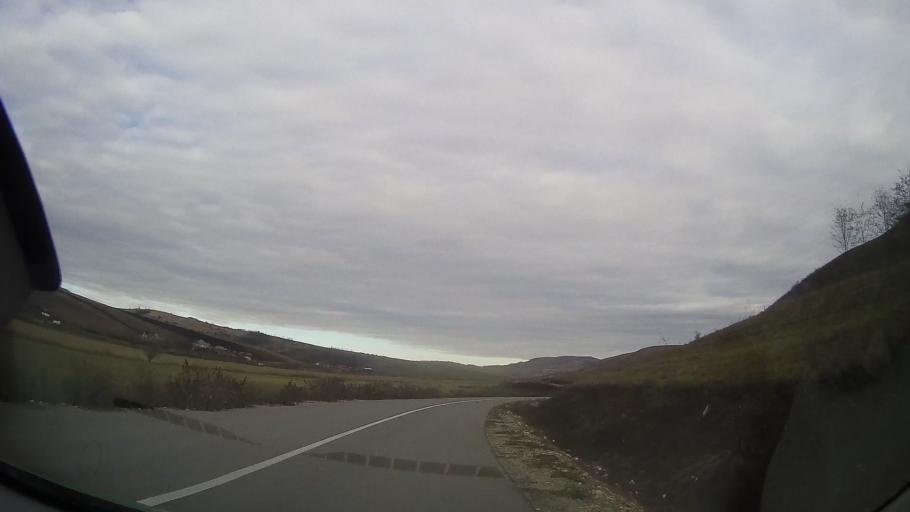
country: RO
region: Bistrita-Nasaud
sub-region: Comuna Silvasu de Campie
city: Silvasu de Campie
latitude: 46.7890
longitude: 24.2864
